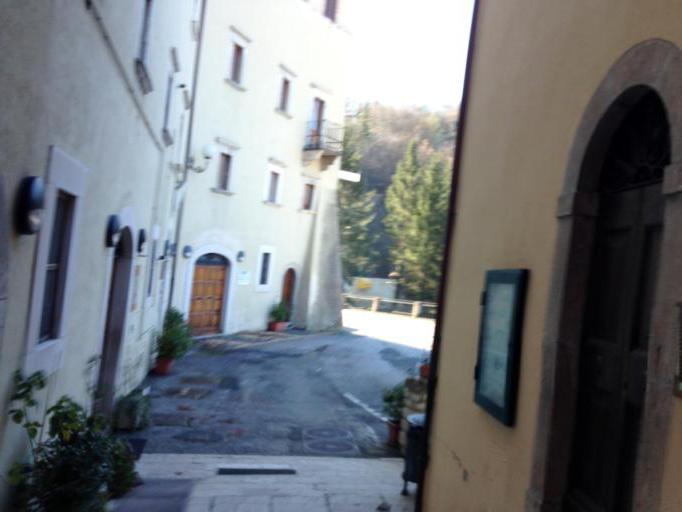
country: IT
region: Umbria
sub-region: Provincia di Perugia
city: Preci
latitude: 42.8787
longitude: 13.0387
